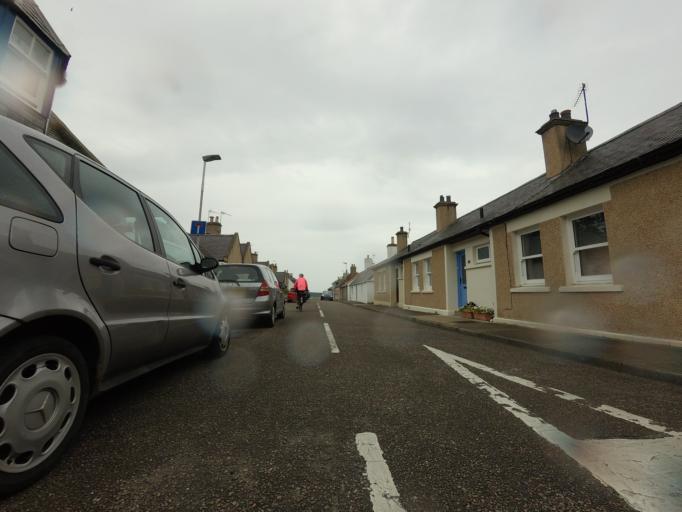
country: GB
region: Scotland
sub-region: Moray
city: Cullen
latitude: 57.6900
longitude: -2.8215
